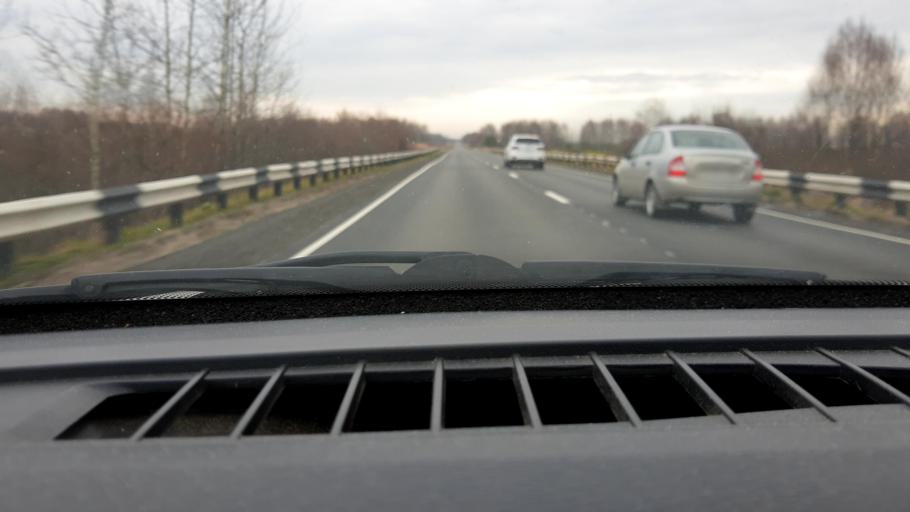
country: RU
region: Nizjnij Novgorod
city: Novaya Balakhna
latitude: 56.5855
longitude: 43.6759
